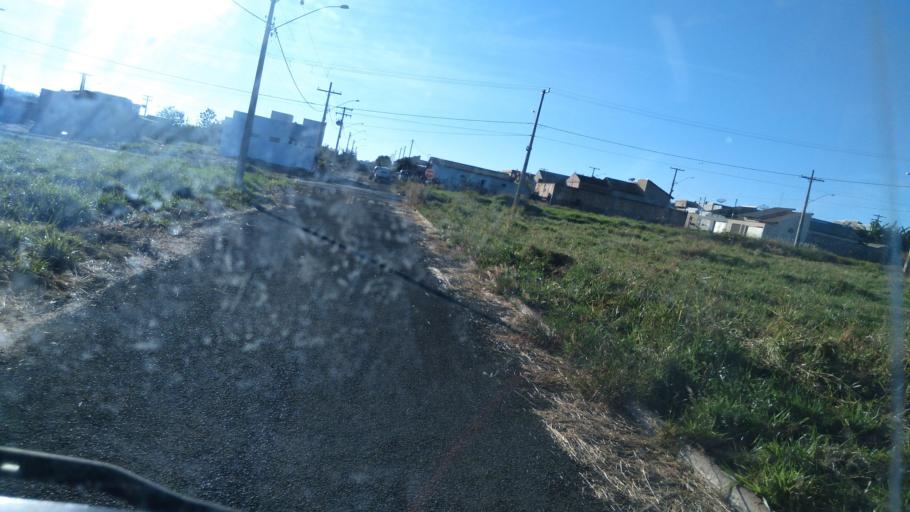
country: BR
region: Goias
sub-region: Mineiros
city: Mineiros
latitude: -17.5423
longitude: -52.5533
